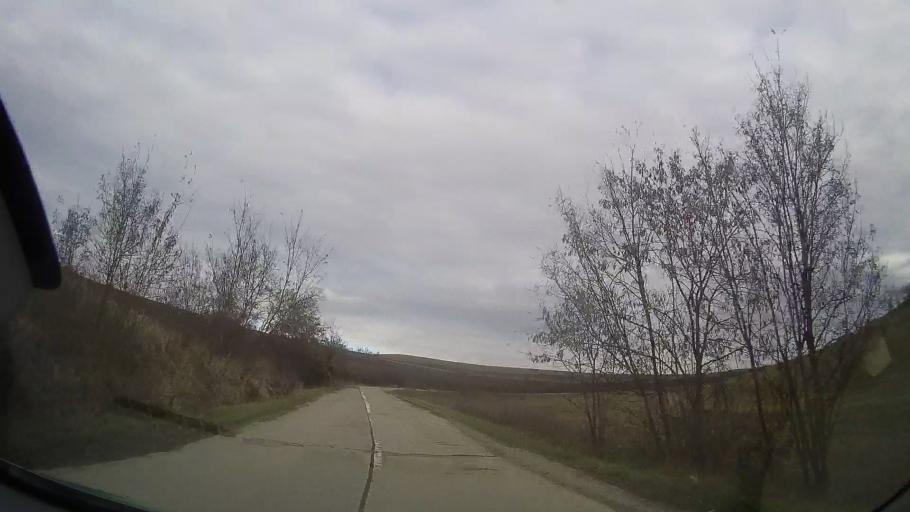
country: RO
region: Bistrita-Nasaud
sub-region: Comuna Micestii de Campie
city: Micestii de Campie
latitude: 46.8482
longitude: 24.3037
